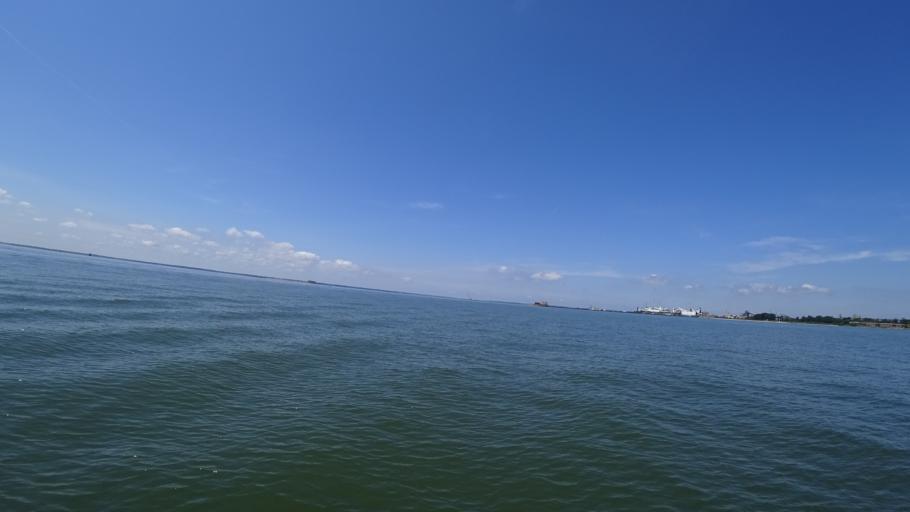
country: US
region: Virginia
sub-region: City of Newport News
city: Newport News
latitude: 36.9676
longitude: -76.3968
